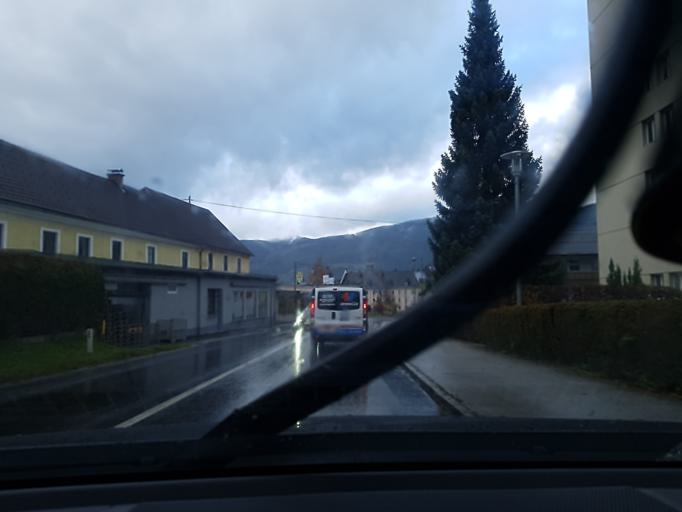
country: AT
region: Styria
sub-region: Politischer Bezirk Liezen
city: Trieben
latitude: 47.4839
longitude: 14.4870
